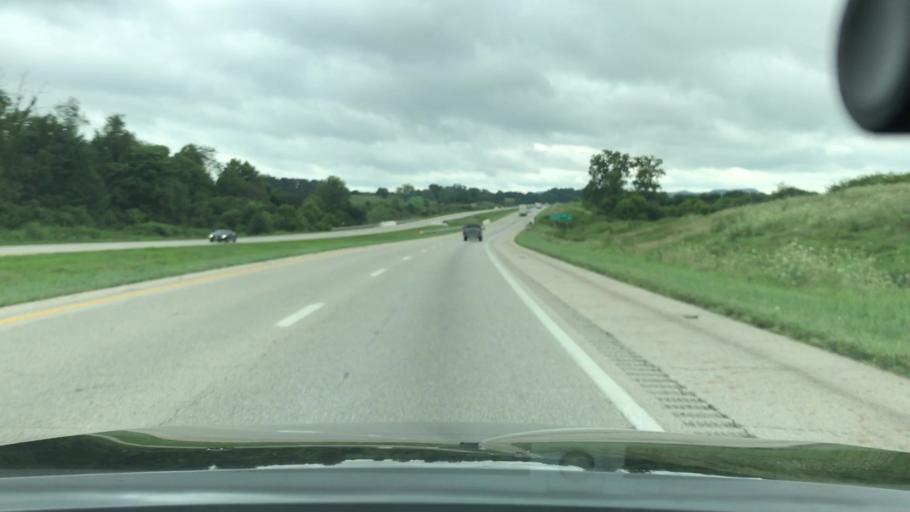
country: US
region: Ohio
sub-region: Ross County
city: Chillicothe
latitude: 39.2920
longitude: -82.8985
